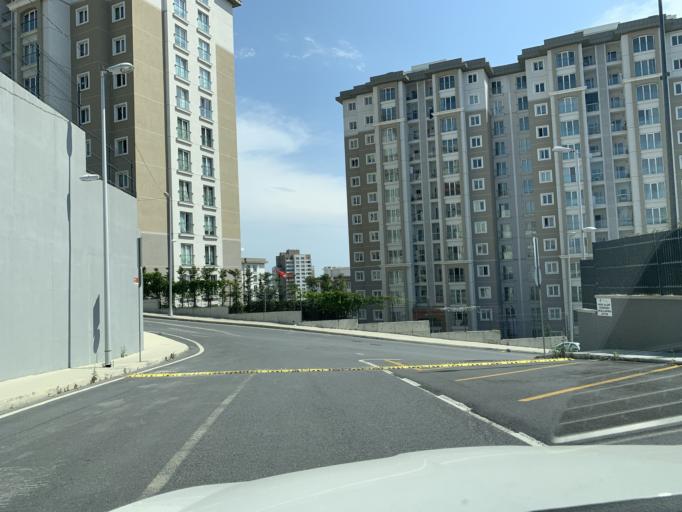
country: TR
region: Istanbul
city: Esenyurt
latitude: 41.0811
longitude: 28.6909
